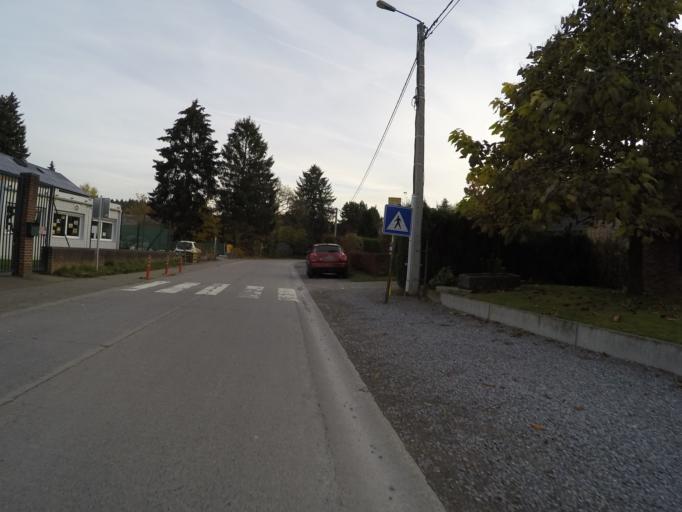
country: BE
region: Wallonia
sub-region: Province du Luxembourg
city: Hotton
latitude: 50.2673
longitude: 5.4428
